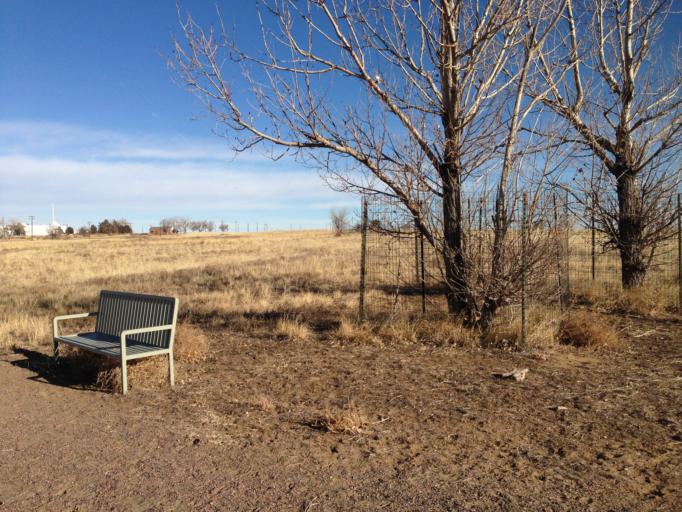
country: US
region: Colorado
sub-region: Adams County
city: Derby
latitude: 39.8257
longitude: -104.8638
